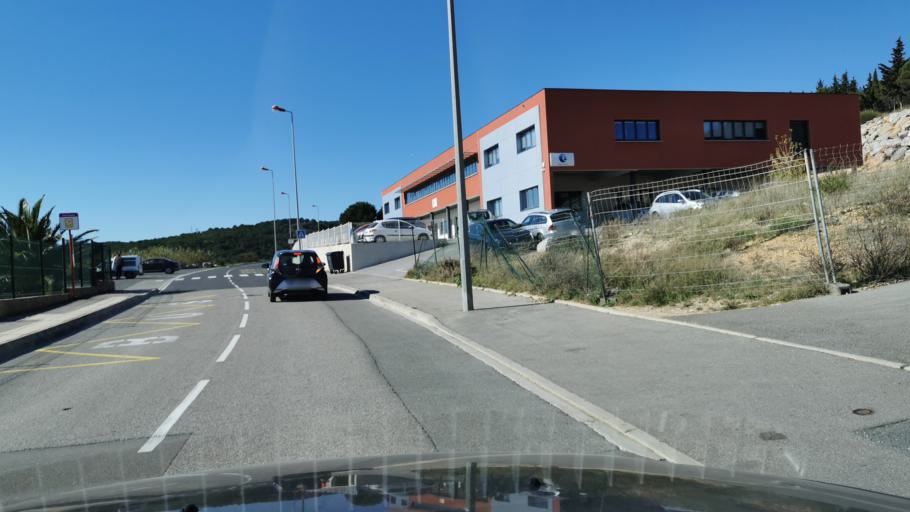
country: FR
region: Languedoc-Roussillon
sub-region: Departement de l'Aude
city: Narbonne
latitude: 43.1533
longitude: 2.9726
